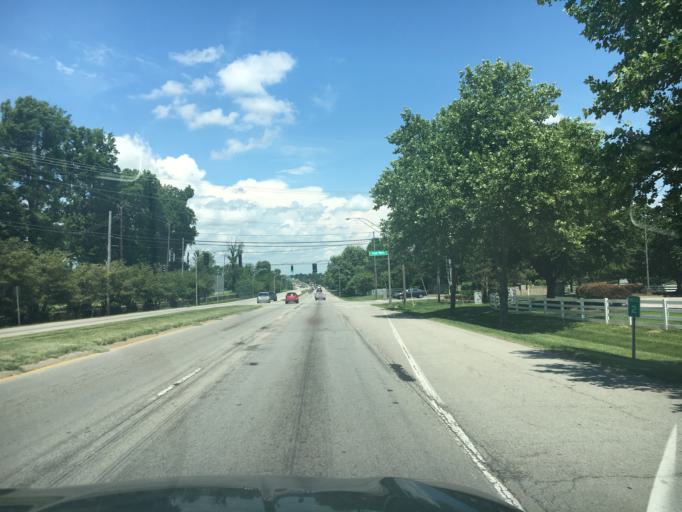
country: US
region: Kentucky
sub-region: Fayette County
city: Lexington-Fayette
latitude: 38.0874
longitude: -84.4896
